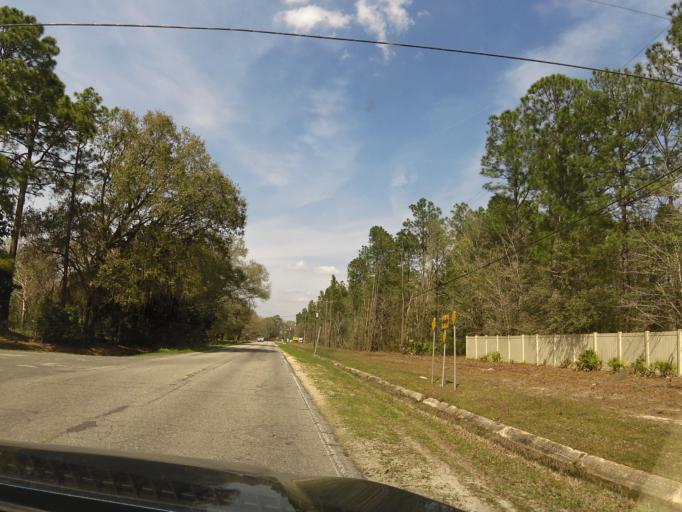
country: US
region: Florida
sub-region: Clay County
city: Middleburg
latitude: 30.1100
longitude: -81.8647
